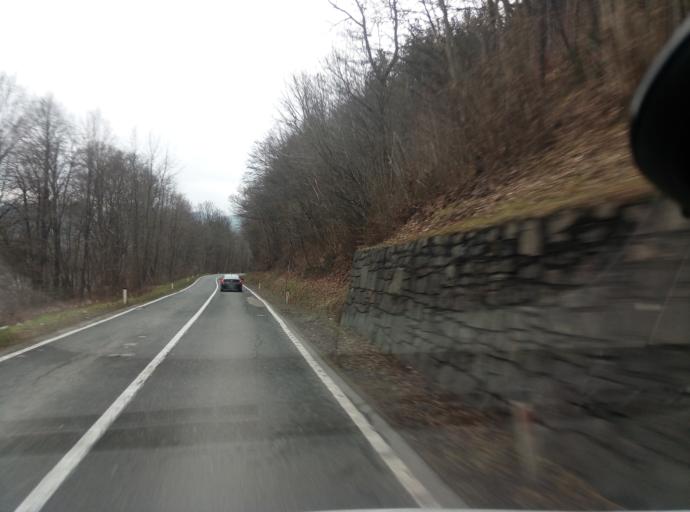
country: SI
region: Smartno pri Litiji
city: Smartno pri Litiji
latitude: 46.0712
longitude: 14.8650
